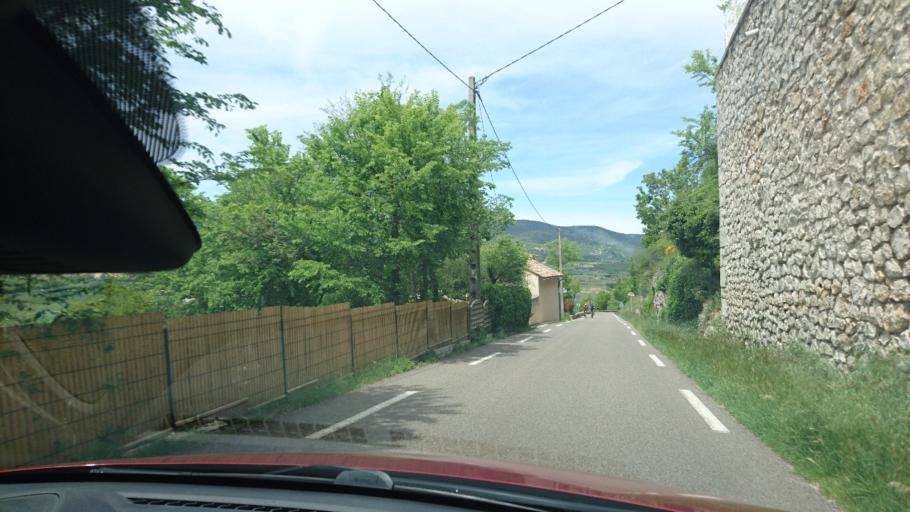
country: FR
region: Provence-Alpes-Cote d'Azur
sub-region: Departement du Vaucluse
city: Sault
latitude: 44.0947
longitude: 5.4081
